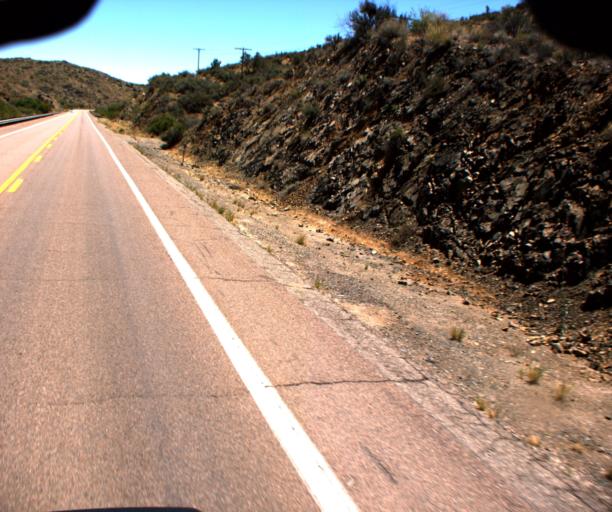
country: US
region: Arizona
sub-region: Yavapai County
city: Bagdad
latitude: 34.5575
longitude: -113.1610
